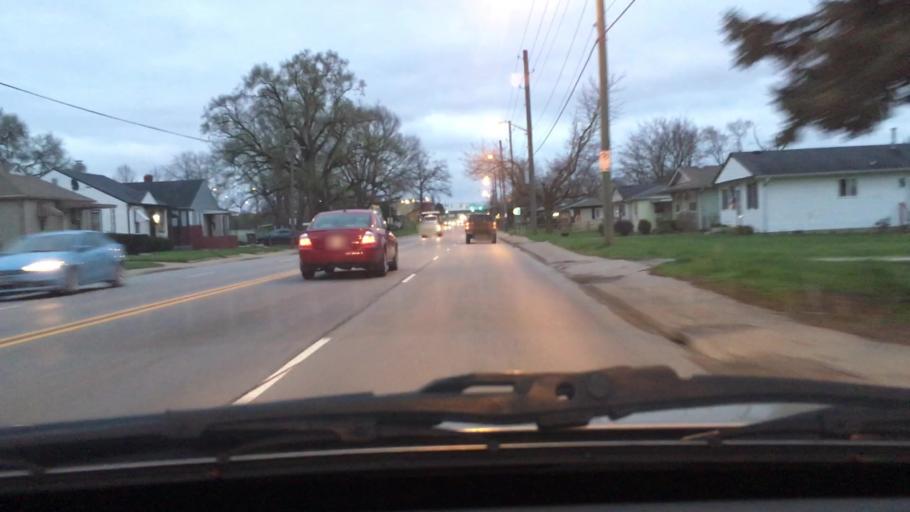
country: US
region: Indiana
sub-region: Marion County
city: Indianapolis
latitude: 39.8061
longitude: -86.1216
